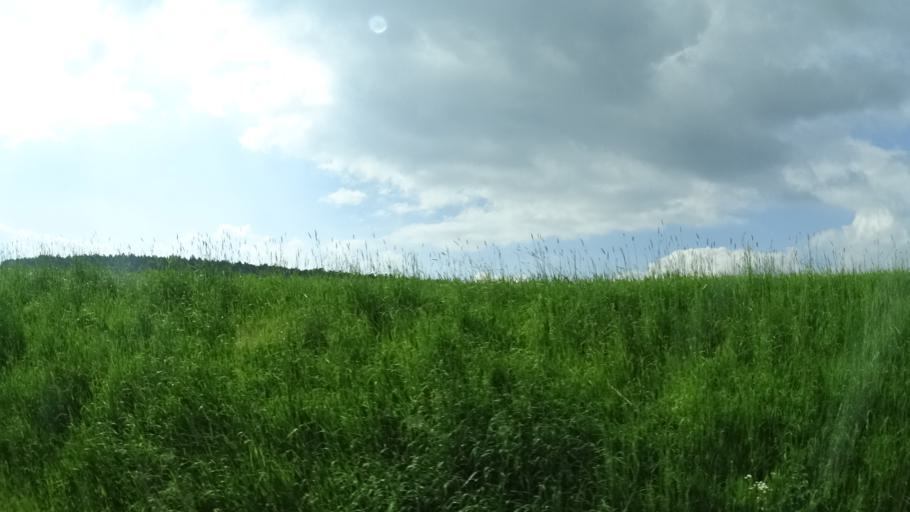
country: DE
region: Bavaria
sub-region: Regierungsbezirk Unterfranken
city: Hammelburg
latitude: 50.1877
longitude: 9.8791
